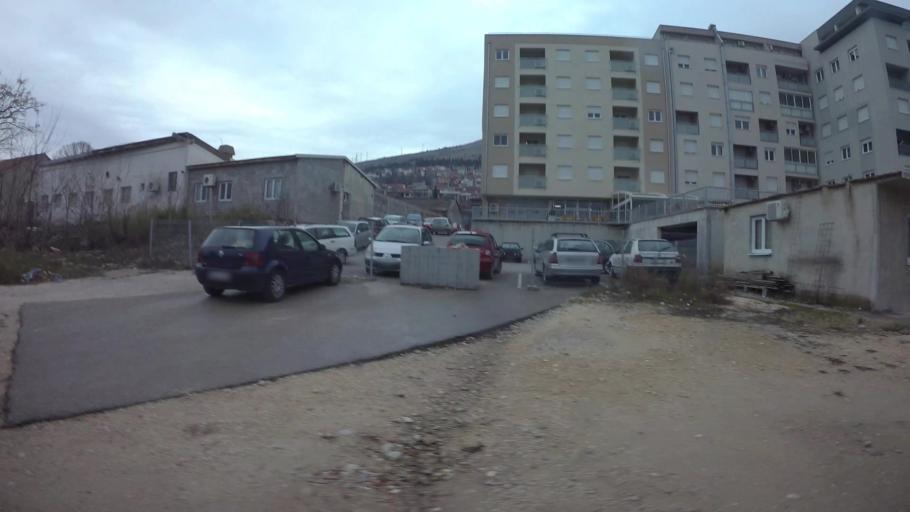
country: BA
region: Federation of Bosnia and Herzegovina
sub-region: Hercegovacko-Bosanski Kanton
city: Mostar
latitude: 43.3503
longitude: 17.8118
